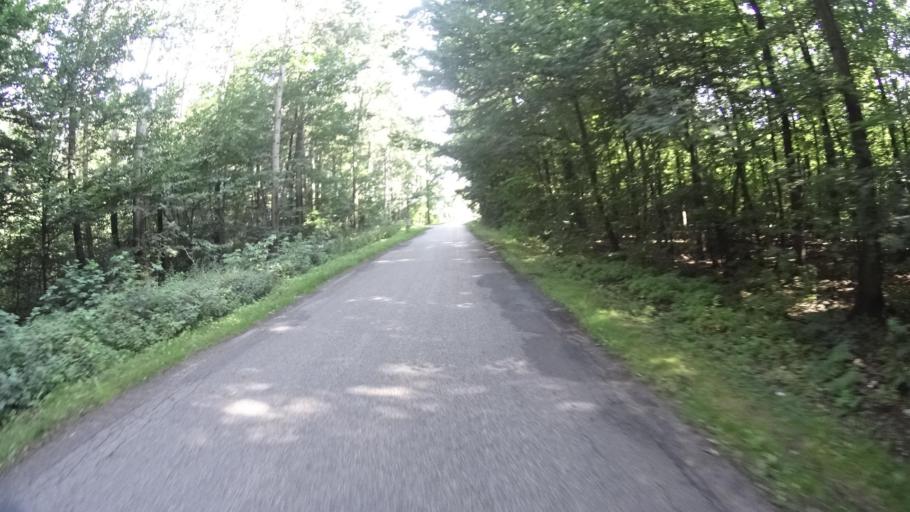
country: PL
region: Masovian Voivodeship
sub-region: Powiat grojecki
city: Goszczyn
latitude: 51.7806
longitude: 20.8540
